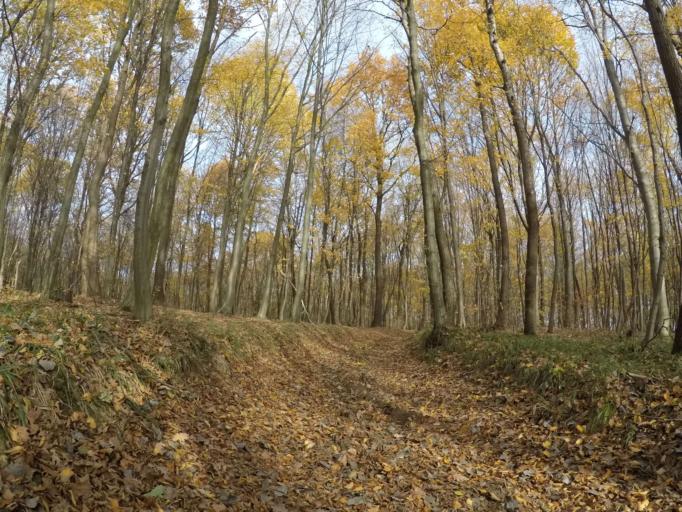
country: SK
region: Presovsky
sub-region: Okres Presov
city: Presov
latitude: 48.9284
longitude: 21.2201
